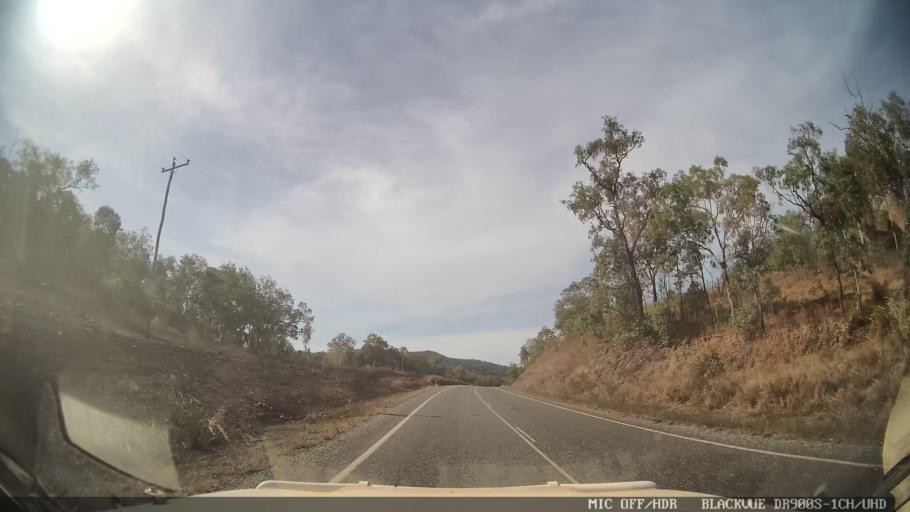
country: AU
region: Queensland
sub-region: Cook
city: Cooktown
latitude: -15.6059
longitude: 145.2221
